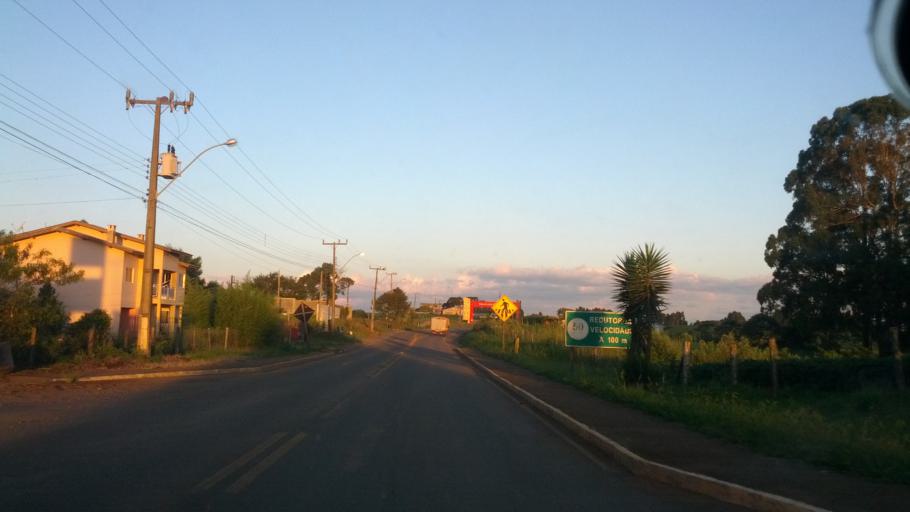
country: BR
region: Rio Grande do Sul
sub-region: Vacaria
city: Estrela
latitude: -27.7969
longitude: -50.8686
